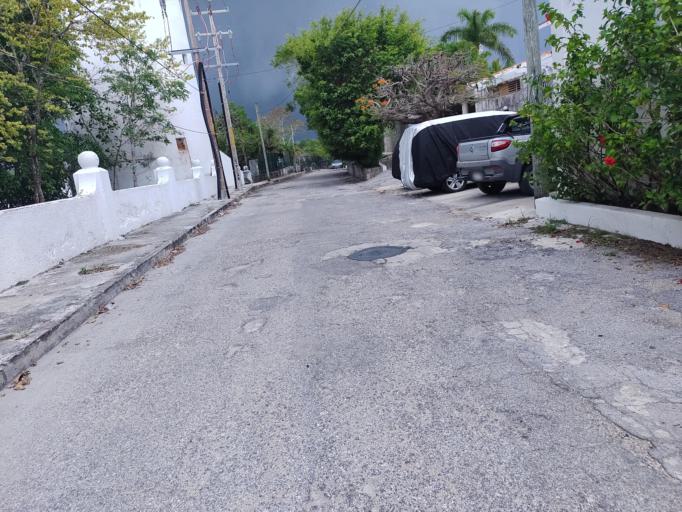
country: MX
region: Quintana Roo
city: San Miguel de Cozumel
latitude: 20.5294
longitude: -86.9399
